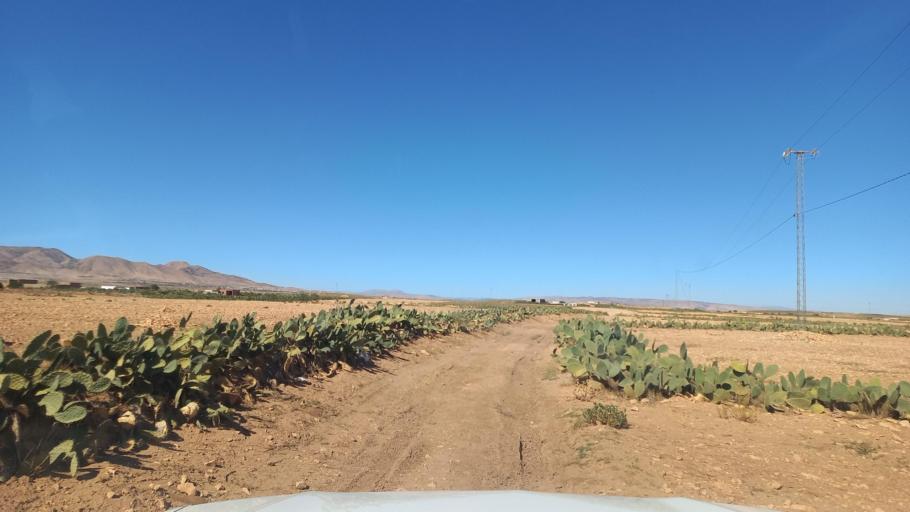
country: TN
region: Al Qasrayn
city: Sbiba
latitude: 35.3843
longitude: 9.0920
